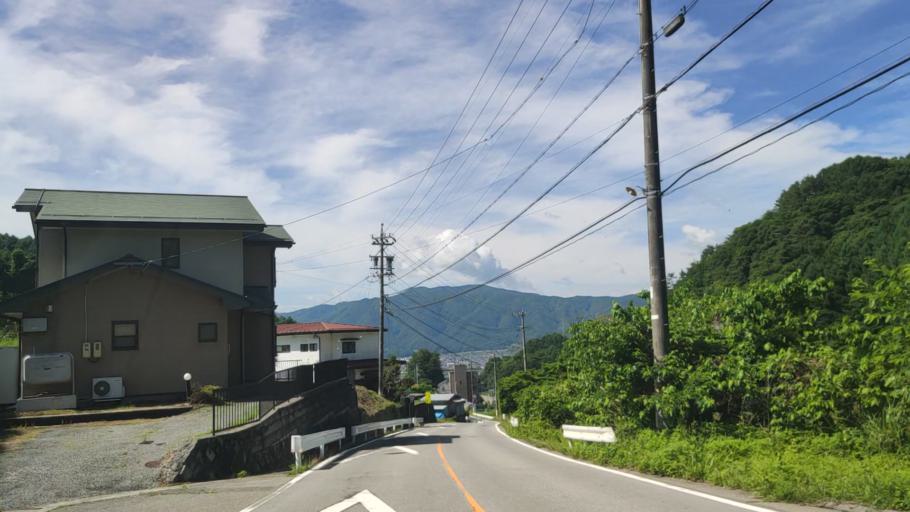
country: JP
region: Nagano
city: Suwa
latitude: 36.0539
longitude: 138.1288
